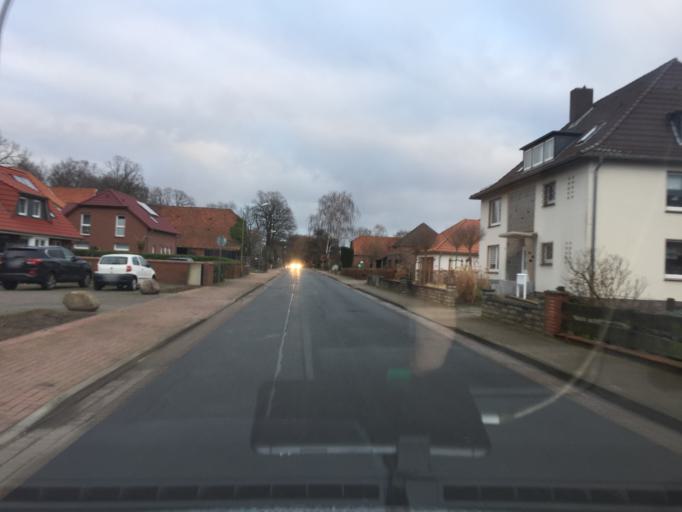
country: DE
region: Lower Saxony
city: Gross Munzel
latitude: 52.4267
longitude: 9.5127
